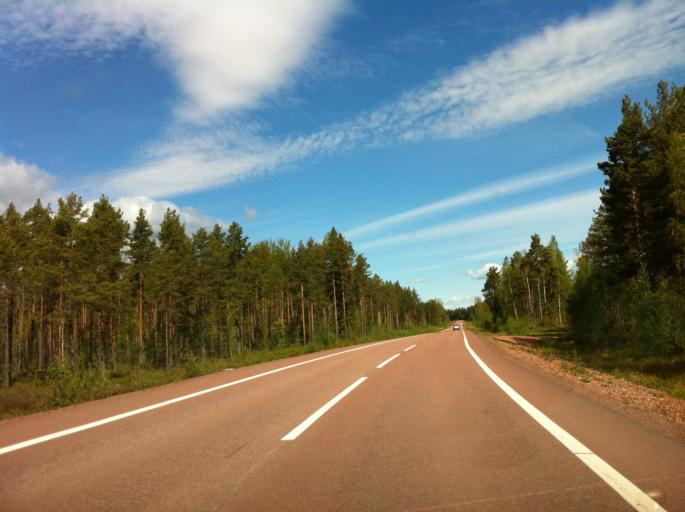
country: SE
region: Dalarna
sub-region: Mora Kommun
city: Mora
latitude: 60.9272
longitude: 14.5680
